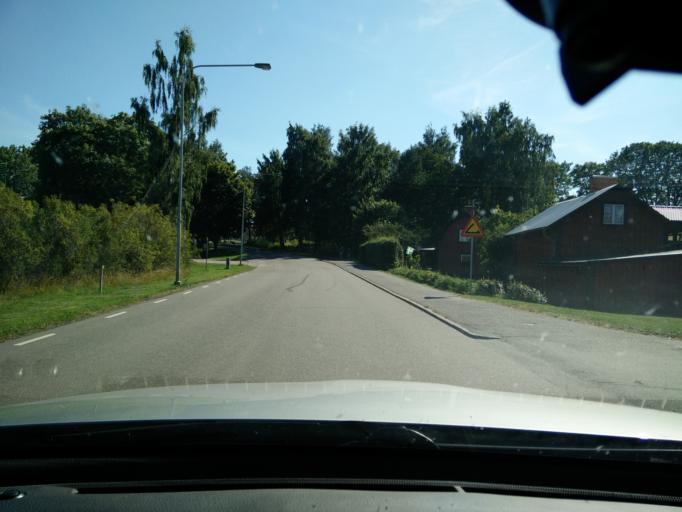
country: SE
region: OEstergoetland
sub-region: Linkopings Kommun
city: Ljungsbro
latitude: 58.5064
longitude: 15.5007
